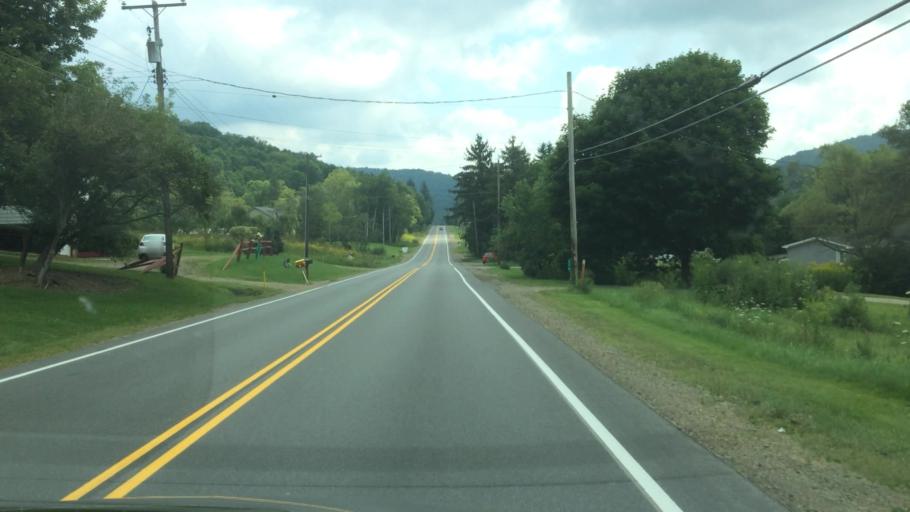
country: US
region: Pennsylvania
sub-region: McKean County
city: Bradford
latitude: 41.9098
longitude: -78.6310
